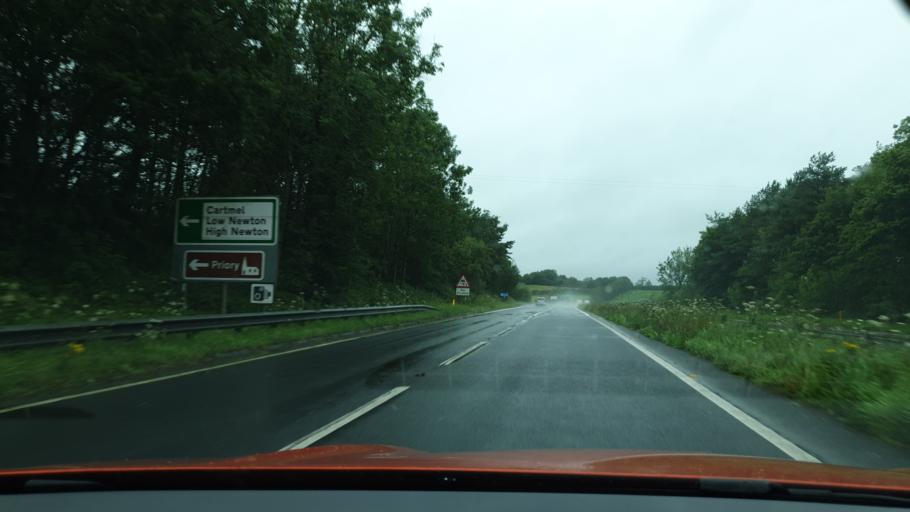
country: GB
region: England
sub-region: Cumbria
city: Grange-over-Sands
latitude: 54.2258
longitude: -2.9100
